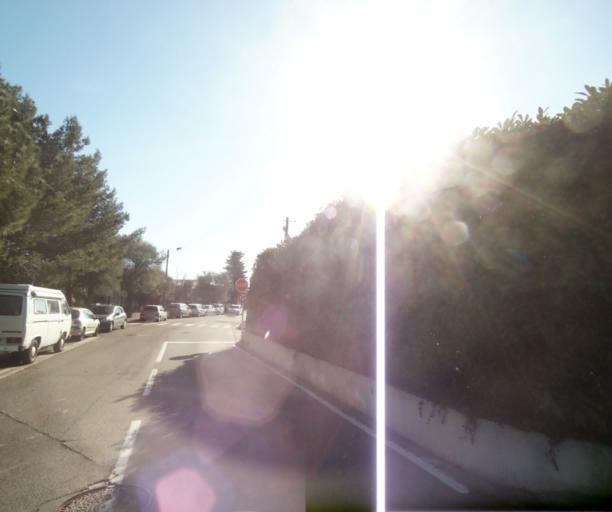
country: FR
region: Provence-Alpes-Cote d'Azur
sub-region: Departement des Alpes-Maritimes
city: Biot
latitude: 43.6066
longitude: 7.1179
